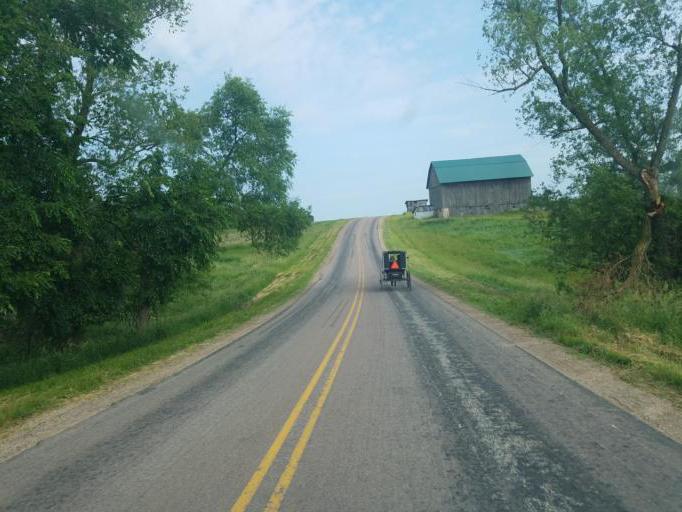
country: US
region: Wisconsin
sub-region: Vernon County
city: Hillsboro
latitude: 43.5977
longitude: -90.4154
